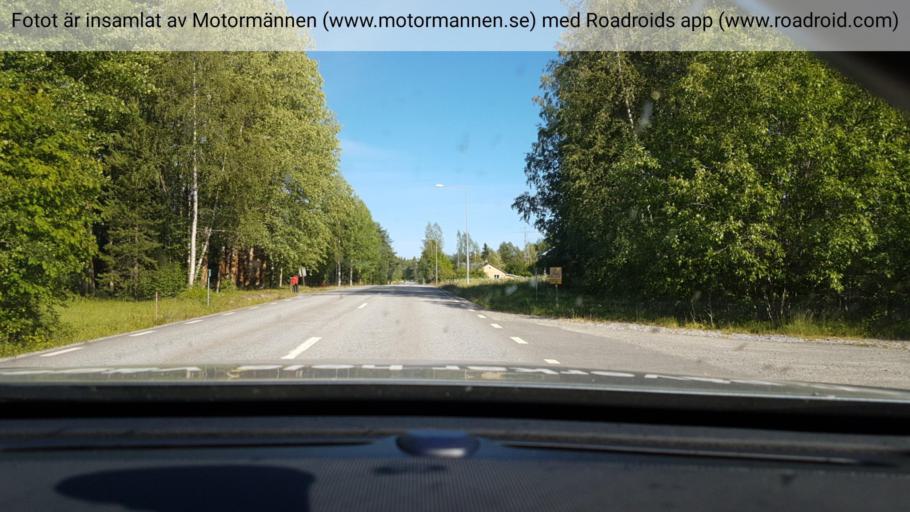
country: SE
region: Vaesterbotten
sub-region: Lycksele Kommun
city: Lycksele
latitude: 64.6338
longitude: 18.5465
